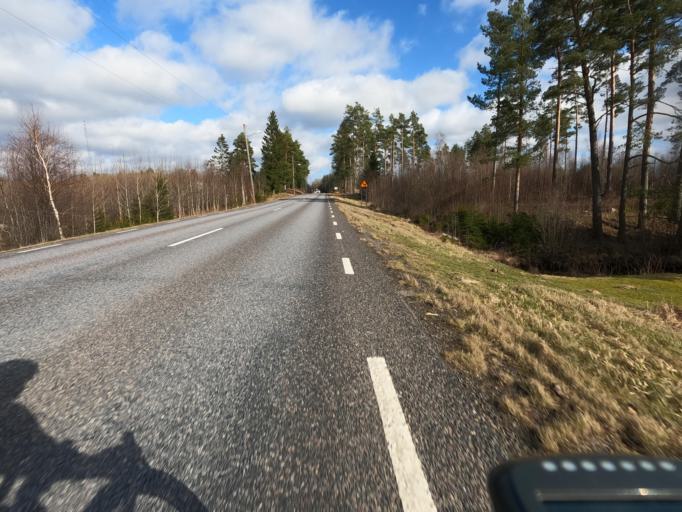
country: SE
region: Kronoberg
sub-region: Alvesta Kommun
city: Vislanda
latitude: 56.7860
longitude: 14.4793
